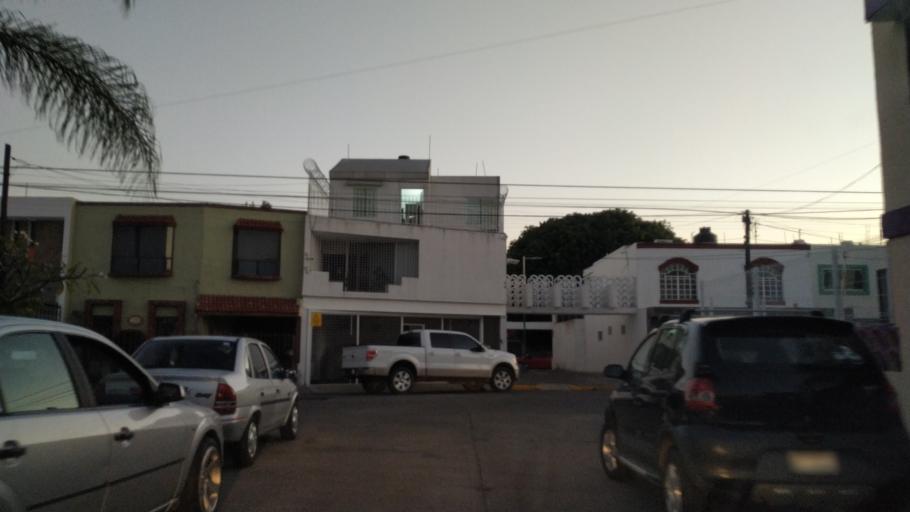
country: MX
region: Jalisco
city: Tlaquepaque
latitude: 20.6535
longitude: -103.3285
